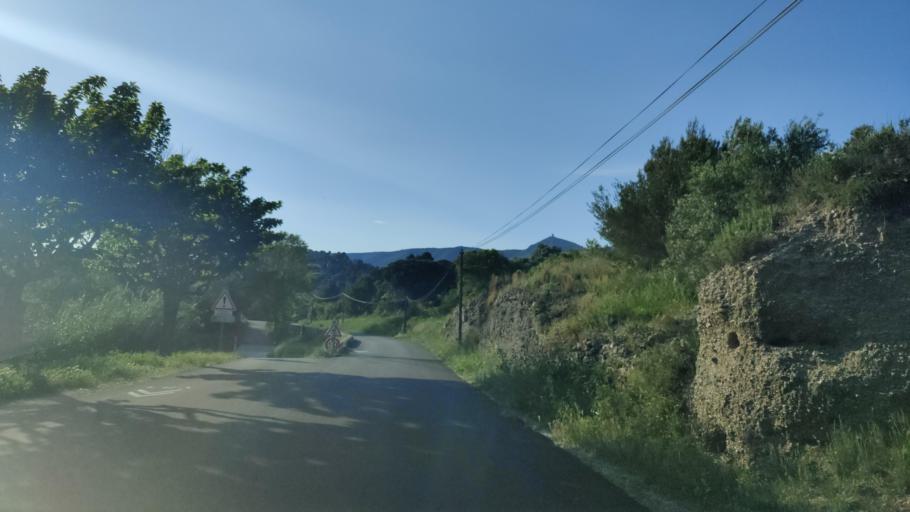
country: FR
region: Languedoc-Roussillon
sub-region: Departement des Pyrenees-Orientales
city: Baixas
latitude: 42.7816
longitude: 2.7806
